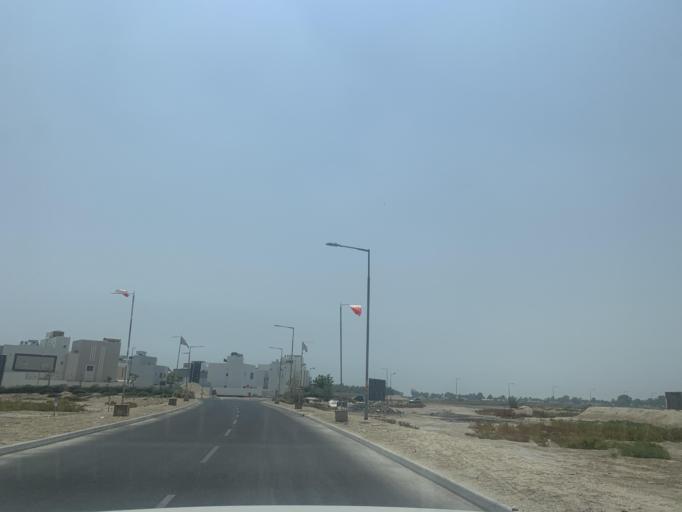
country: BH
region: Central Governorate
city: Madinat Hamad
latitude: 26.1338
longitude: 50.4687
